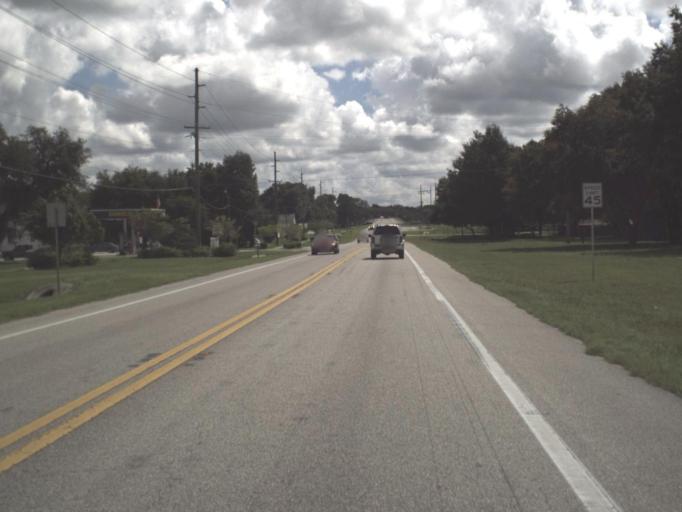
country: US
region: Florida
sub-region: Polk County
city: Polk City
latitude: 28.1791
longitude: -81.8338
